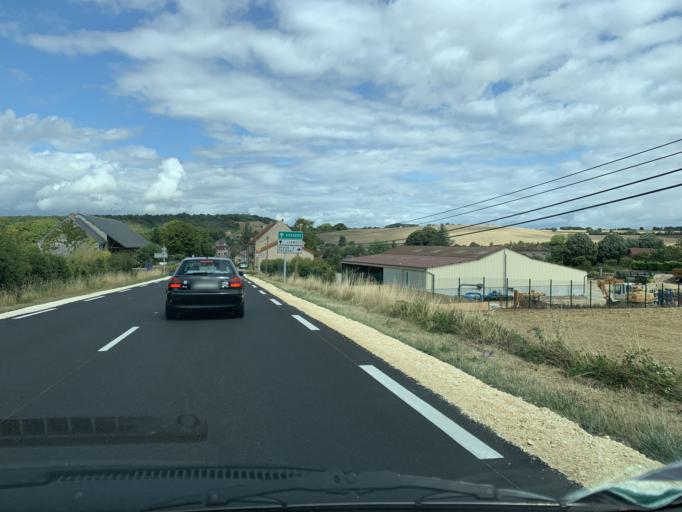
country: FR
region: Bourgogne
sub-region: Departement de la Nievre
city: Varzy
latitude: 47.3525
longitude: 3.3817
